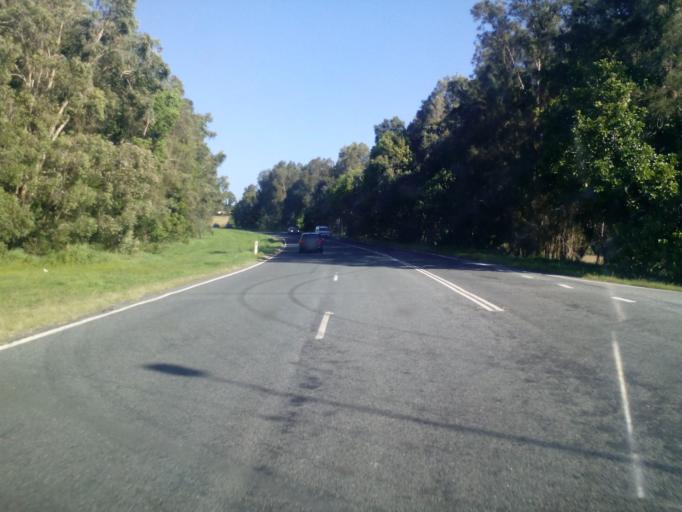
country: AU
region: New South Wales
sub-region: Tweed
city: Kingscliff
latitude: -28.2571
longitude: 153.5598
